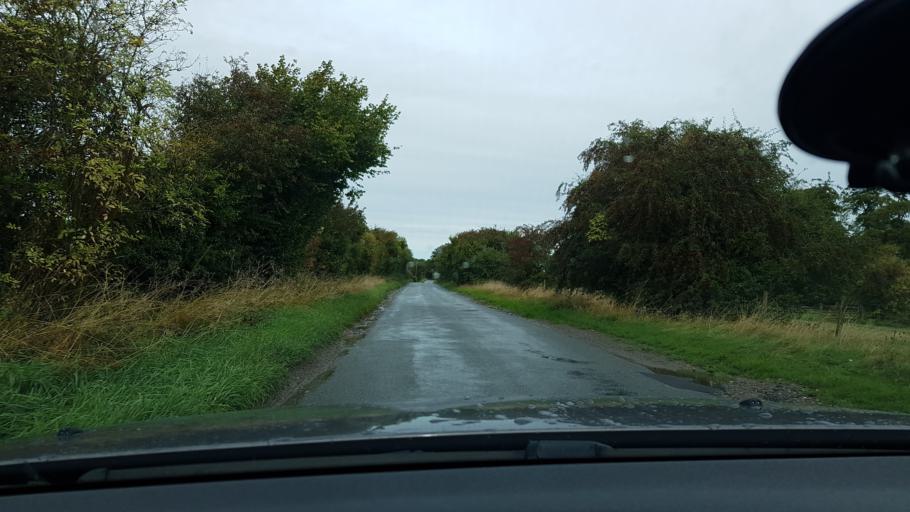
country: GB
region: England
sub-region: West Berkshire
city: Lambourn
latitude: 51.5344
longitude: -1.5278
